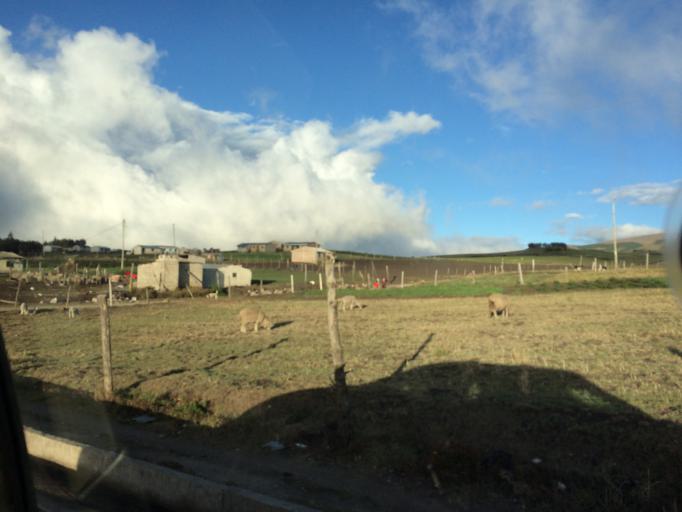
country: EC
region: Chimborazo
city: Alausi
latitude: -2.1327
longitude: -78.7190
